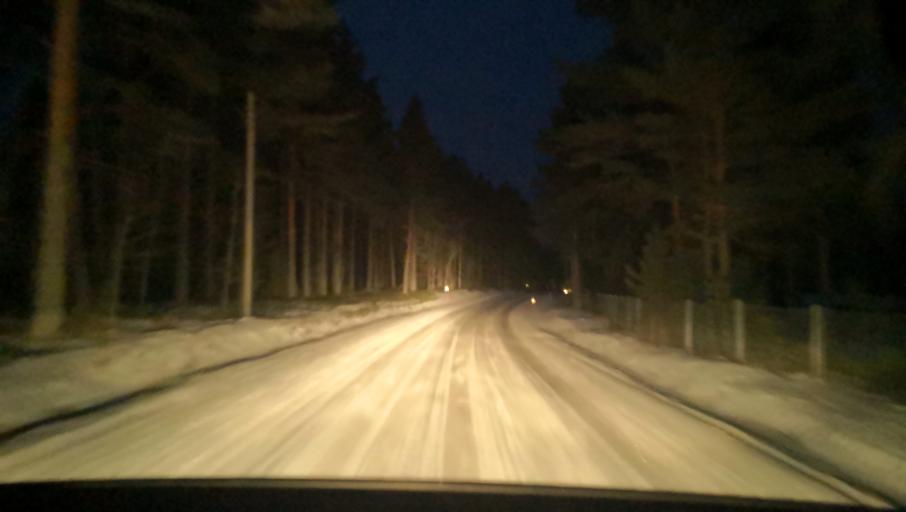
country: SE
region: Uppsala
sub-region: Heby Kommun
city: Tarnsjo
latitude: 60.2837
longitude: 16.8051
